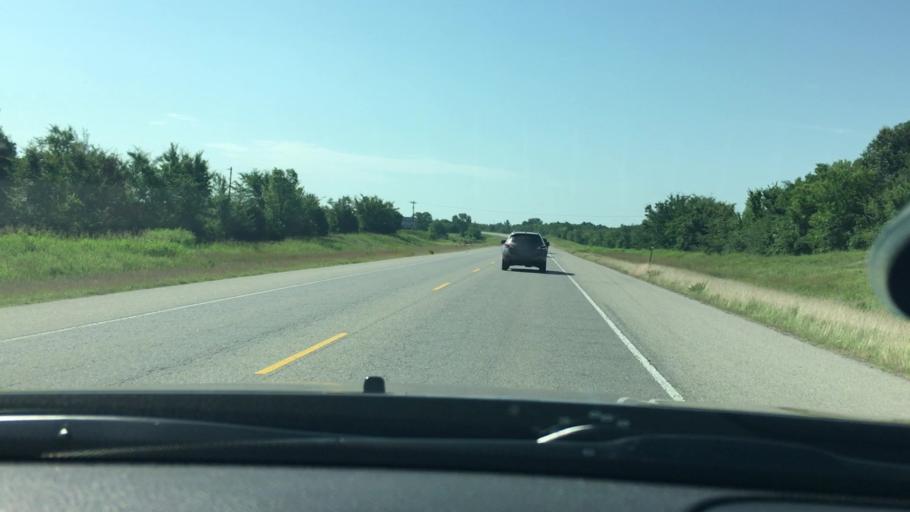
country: US
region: Oklahoma
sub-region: Pontotoc County
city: Ada
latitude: 34.6526
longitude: -96.5553
